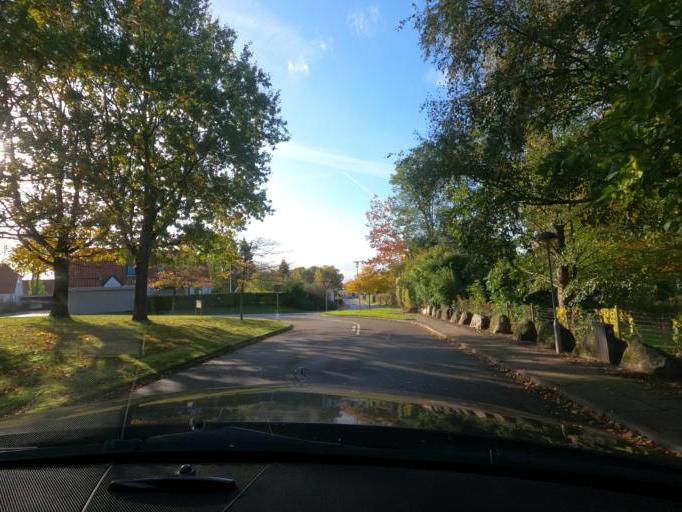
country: DK
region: South Denmark
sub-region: Sonderborg Kommune
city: Dybbol
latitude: 54.9193
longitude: 9.7243
